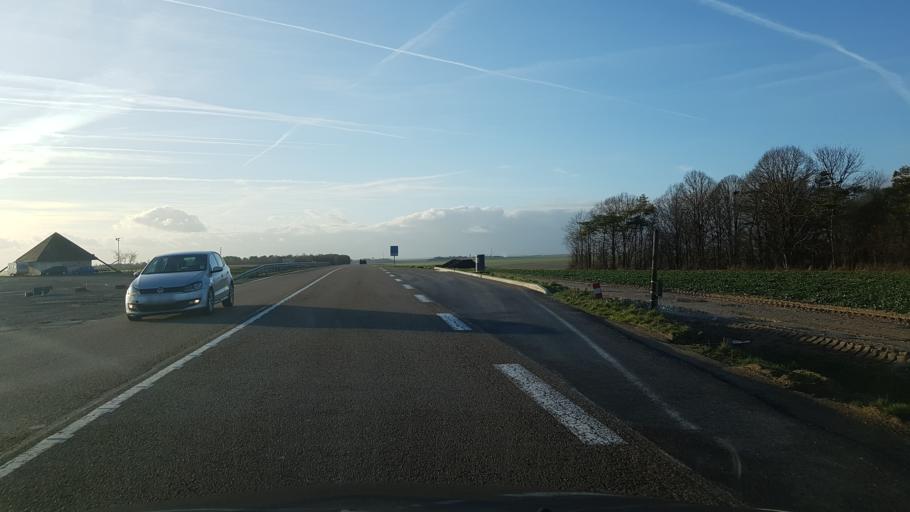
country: FR
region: Champagne-Ardenne
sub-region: Departement de l'Aube
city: Mailly-le-Camp
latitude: 48.7338
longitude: 4.2797
